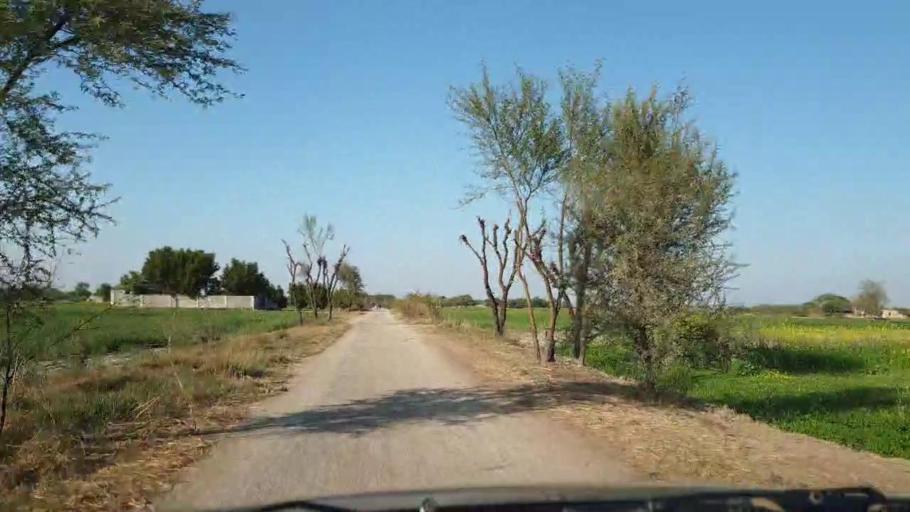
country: PK
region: Sindh
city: Khadro
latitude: 26.2108
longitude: 68.7543
